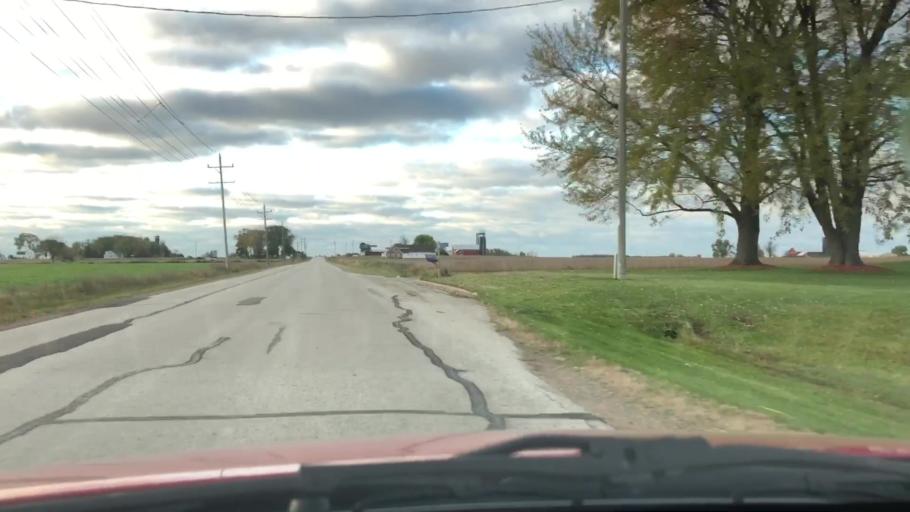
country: US
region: Wisconsin
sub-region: Outagamie County
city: Seymour
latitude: 44.5062
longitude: -88.3105
